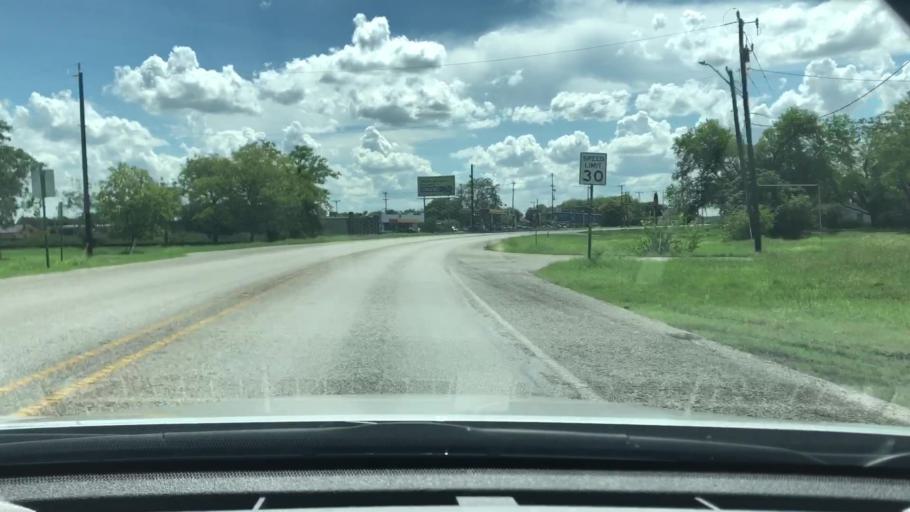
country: US
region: Texas
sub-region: Bexar County
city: Converse
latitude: 29.5197
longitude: -98.3144
